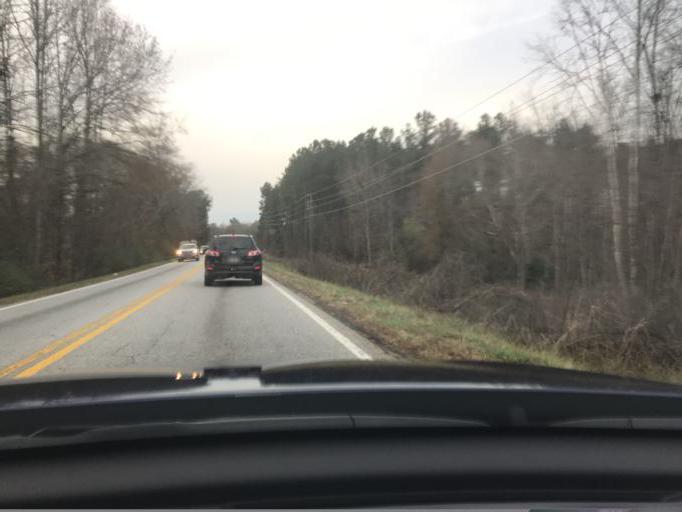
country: US
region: Georgia
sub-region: Newton County
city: Porterdale
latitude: 33.6051
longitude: -83.9174
